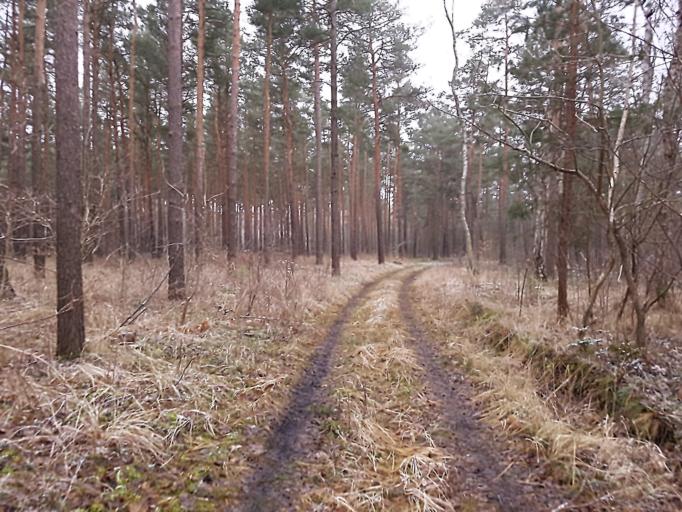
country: DE
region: Brandenburg
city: Schilda
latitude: 51.5874
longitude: 13.3995
